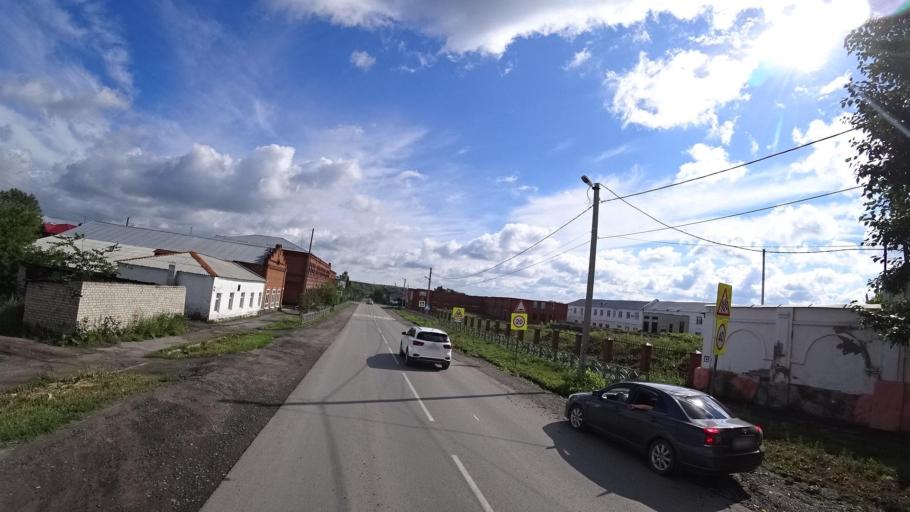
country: RU
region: Sverdlovsk
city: Kamyshlov
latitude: 56.8459
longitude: 62.6989
